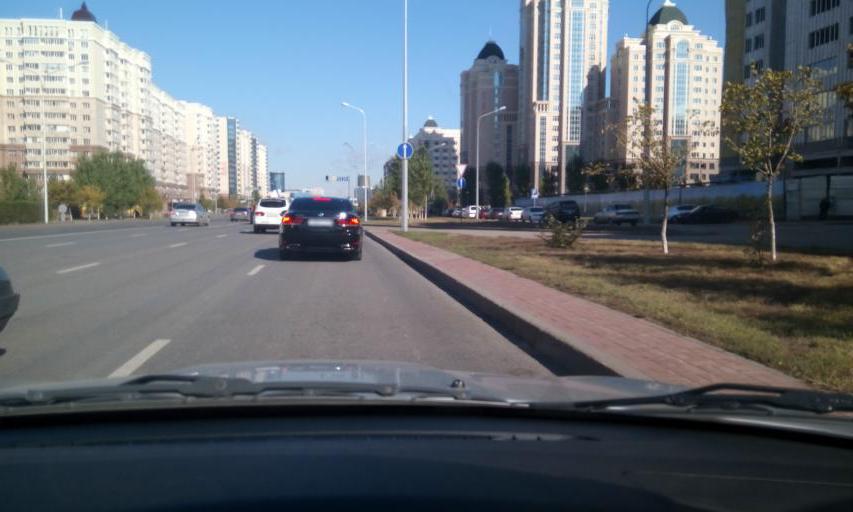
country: KZ
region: Astana Qalasy
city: Astana
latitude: 51.1117
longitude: 71.4329
